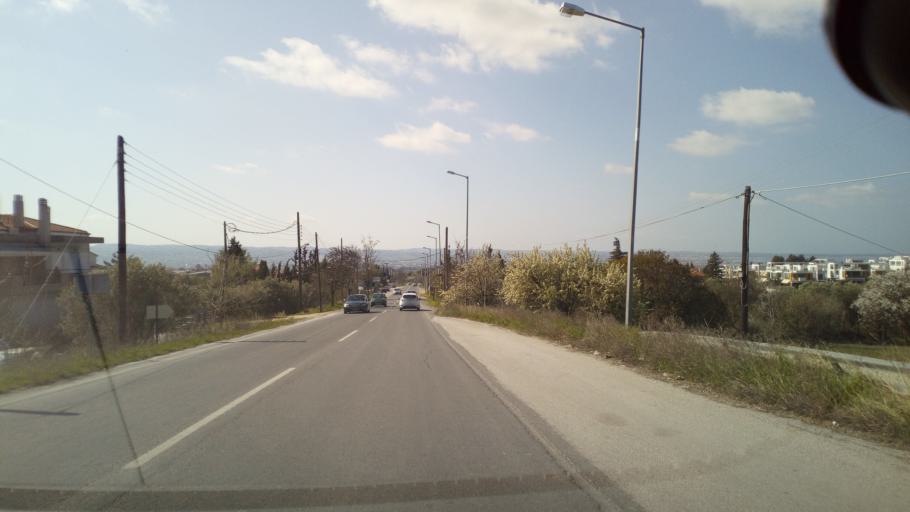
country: GR
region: Central Macedonia
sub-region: Nomos Thessalonikis
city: Thermi
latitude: 40.5601
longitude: 23.0222
